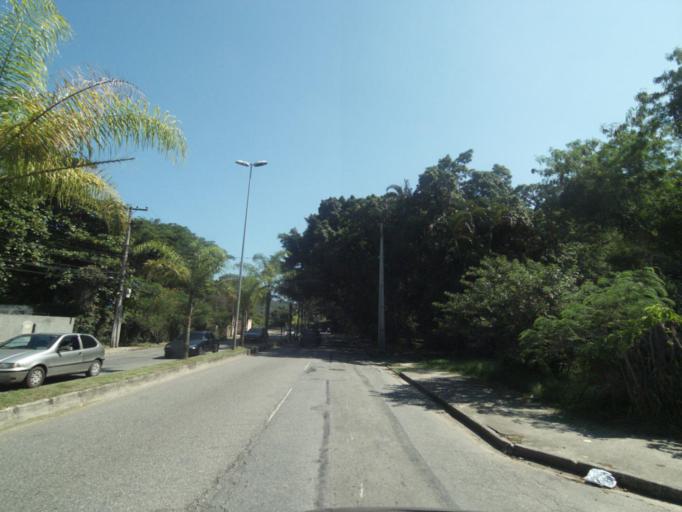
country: BR
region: Rio de Janeiro
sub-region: Niteroi
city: Niteroi
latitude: -22.8942
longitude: -43.0376
